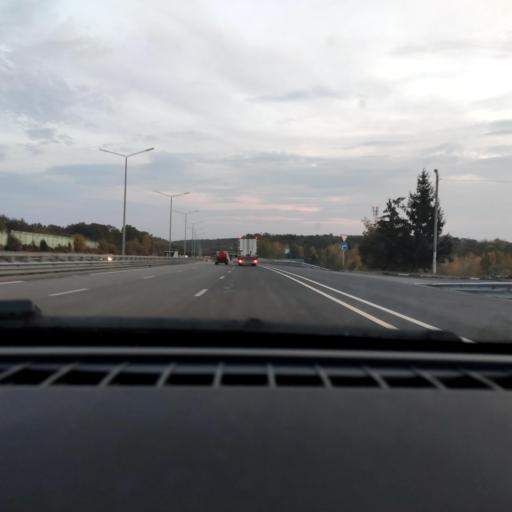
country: RU
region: Voronezj
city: Podgornoye
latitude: 51.8126
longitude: 39.2520
